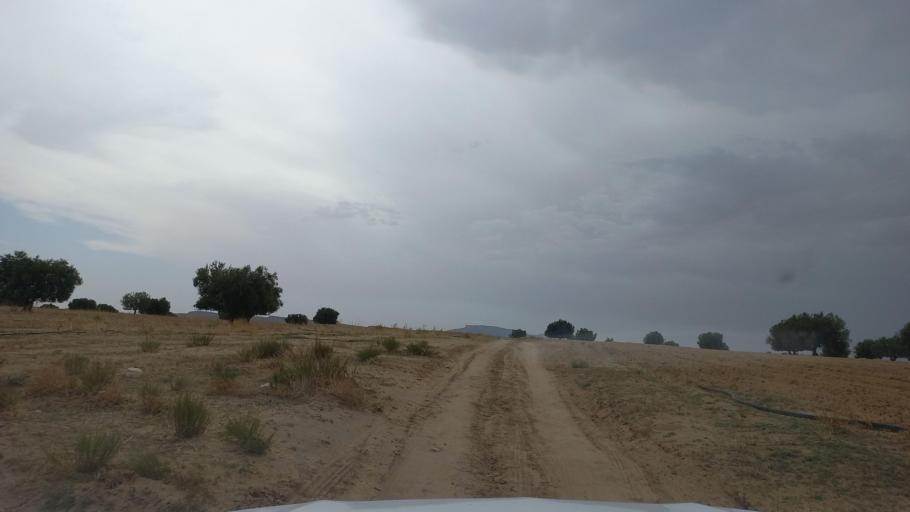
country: TN
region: Al Qasrayn
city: Kasserine
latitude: 35.2351
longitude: 9.0146
